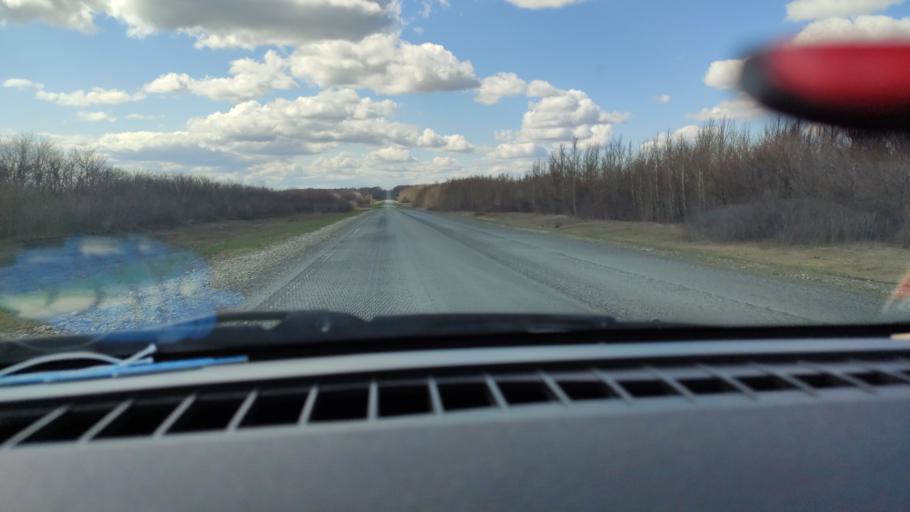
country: RU
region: Saratov
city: Dukhovnitskoye
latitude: 52.6960
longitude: 48.2494
